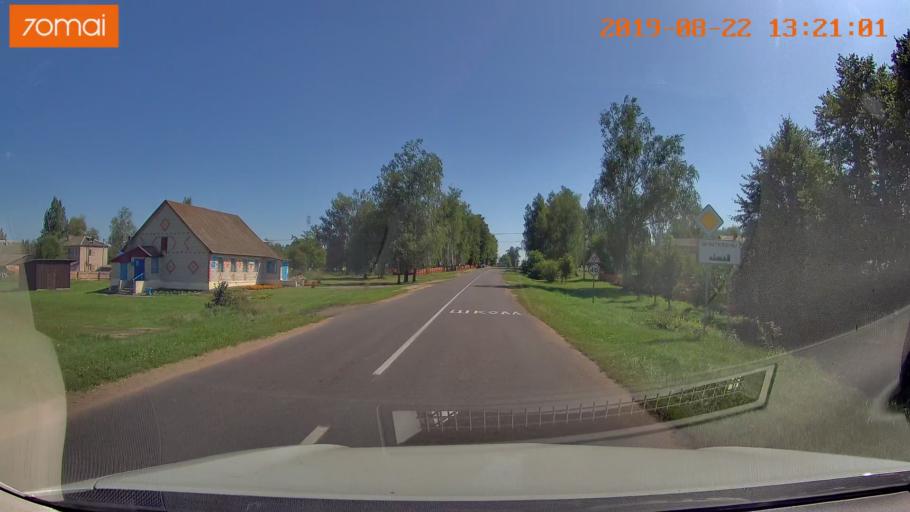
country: BY
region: Minsk
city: Urechcha
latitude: 53.2268
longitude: 27.9760
